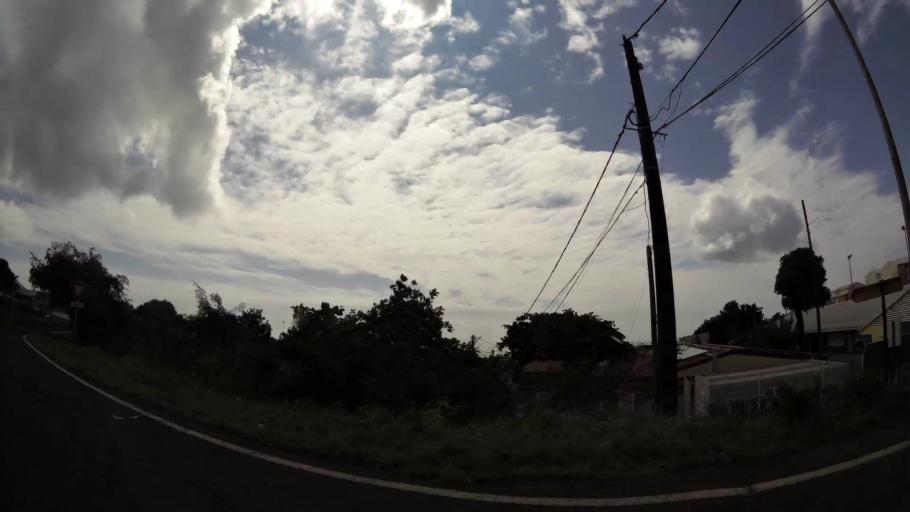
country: GP
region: Guadeloupe
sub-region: Guadeloupe
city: Basse-Terre
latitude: 16.0007
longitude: -61.7237
